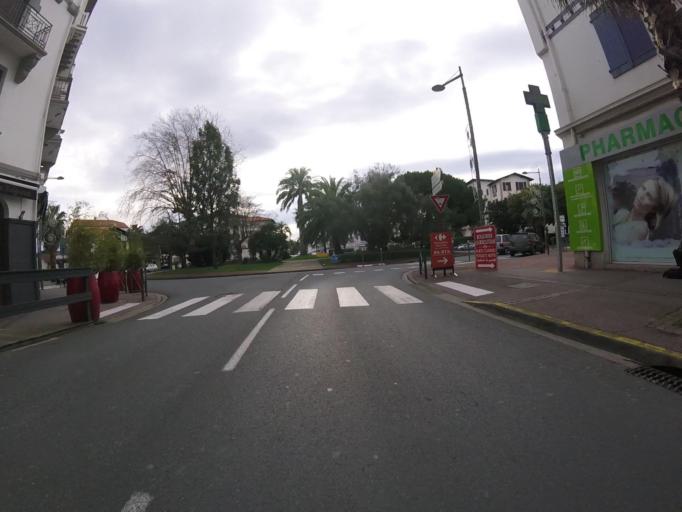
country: FR
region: Aquitaine
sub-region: Departement des Pyrenees-Atlantiques
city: Hendaye
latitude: 43.3720
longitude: -1.7734
